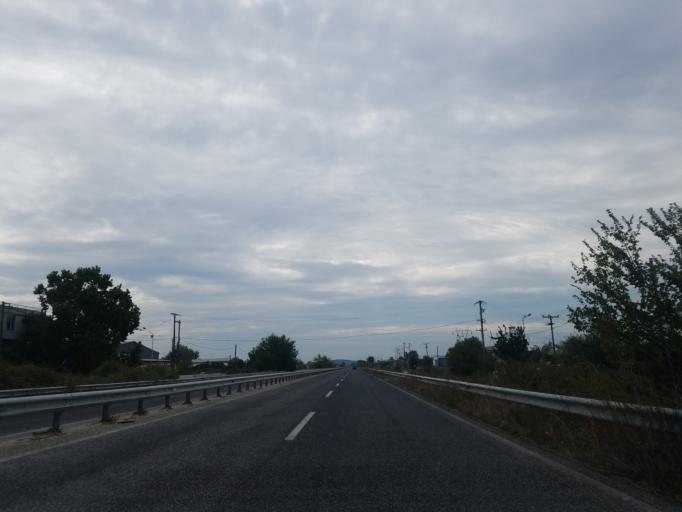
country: GR
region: Thessaly
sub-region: Trikala
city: Vasiliki
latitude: 39.6125
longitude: 21.7195
